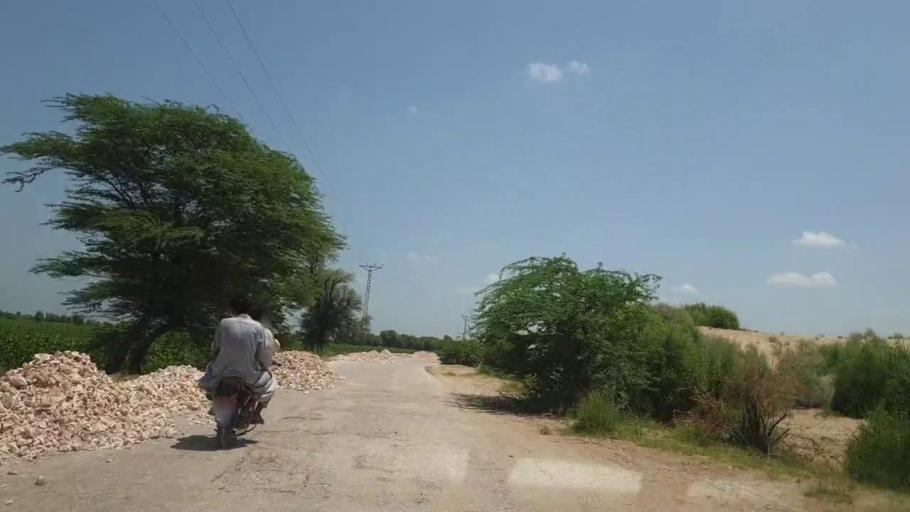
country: PK
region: Sindh
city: Pano Aqil
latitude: 27.6653
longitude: 69.2065
